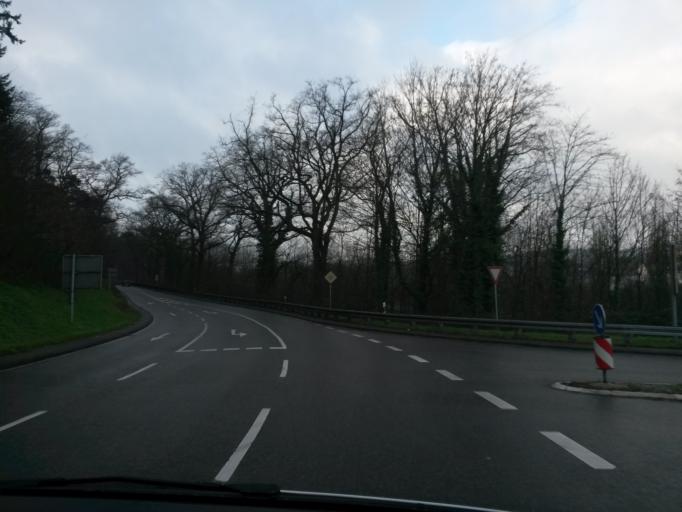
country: DE
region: Baden-Wuerttemberg
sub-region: Karlsruhe Region
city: Eutingen
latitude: 48.8947
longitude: 8.7285
